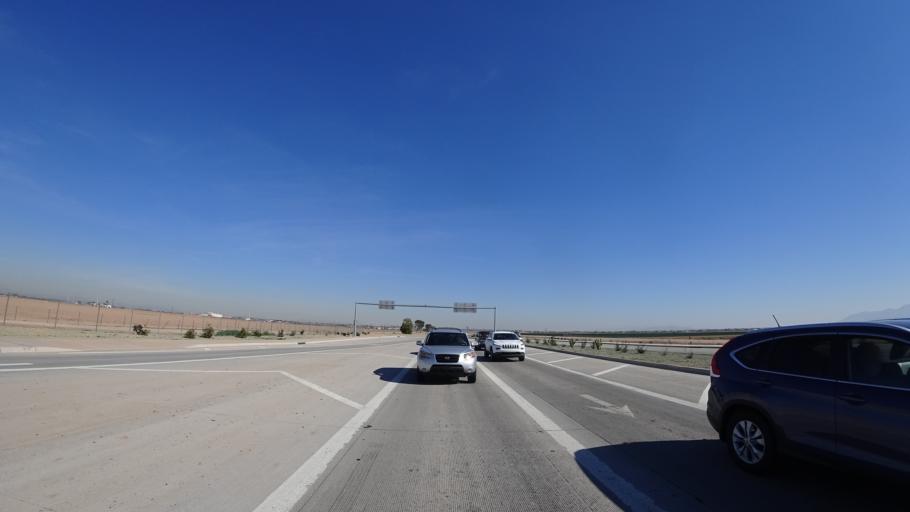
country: US
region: Arizona
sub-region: Maricopa County
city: Citrus Park
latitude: 33.5083
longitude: -112.4178
